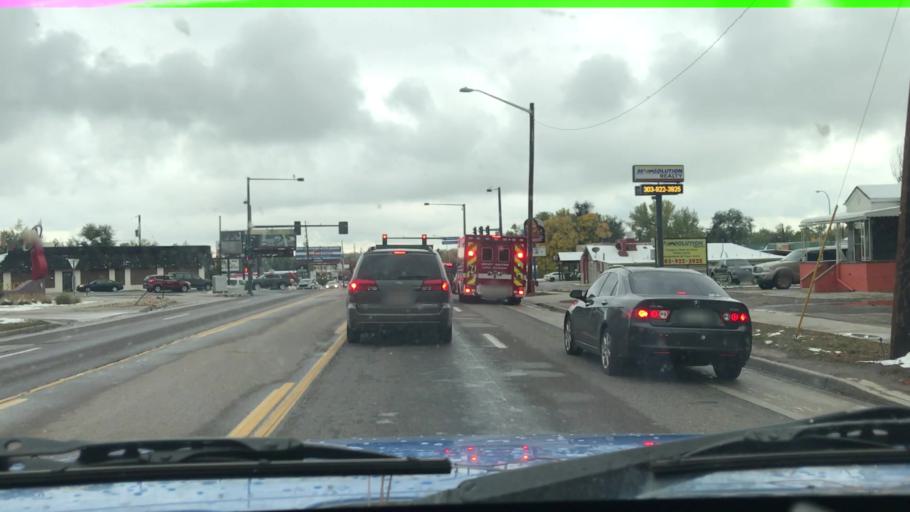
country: US
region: Colorado
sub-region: Jefferson County
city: Lakewood
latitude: 39.6978
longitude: -105.0533
